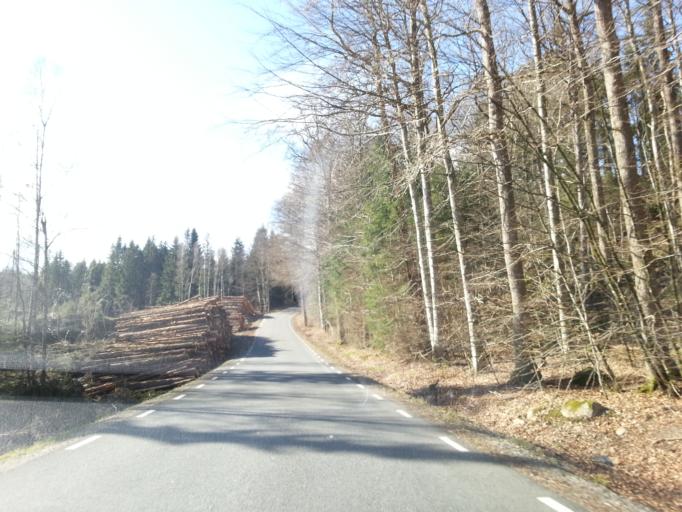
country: SE
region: Vaestra Goetaland
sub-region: Kungalvs Kommun
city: Diserod
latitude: 57.9618
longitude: 12.0086
